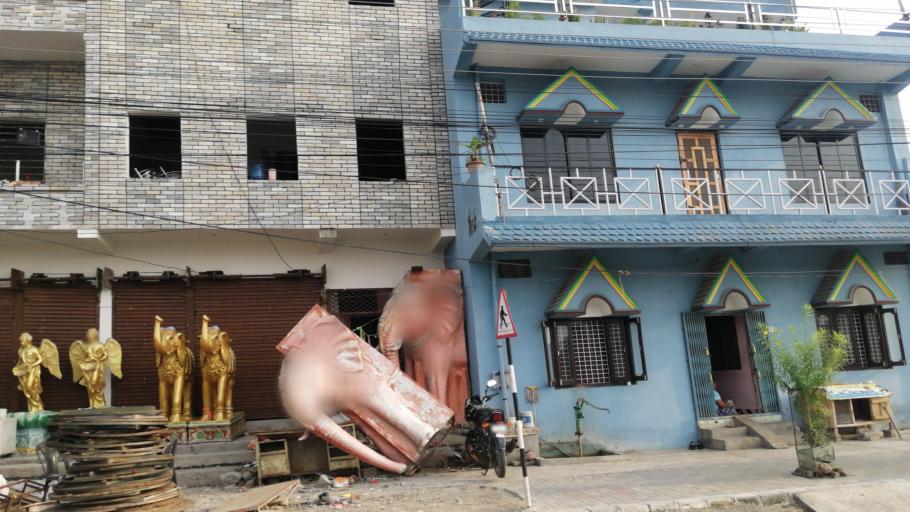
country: NP
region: Western Region
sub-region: Lumbini Zone
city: Bhairahawa
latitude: 27.4980
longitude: 83.4526
